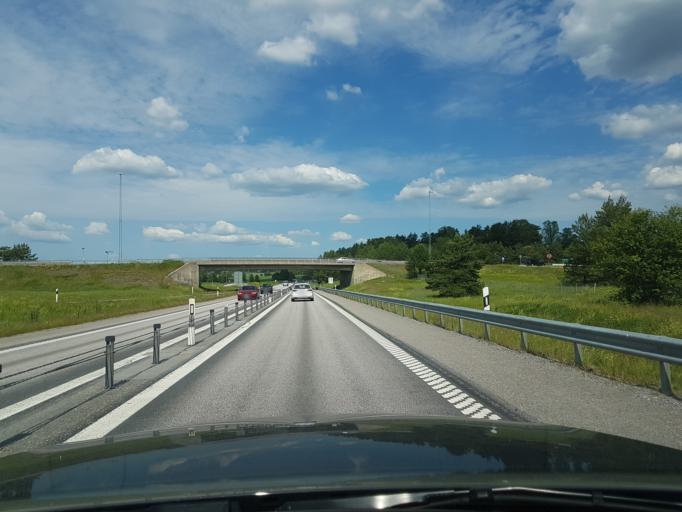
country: SE
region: Stockholm
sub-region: Osterakers Kommun
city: Akersberga
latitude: 59.5588
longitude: 18.2314
